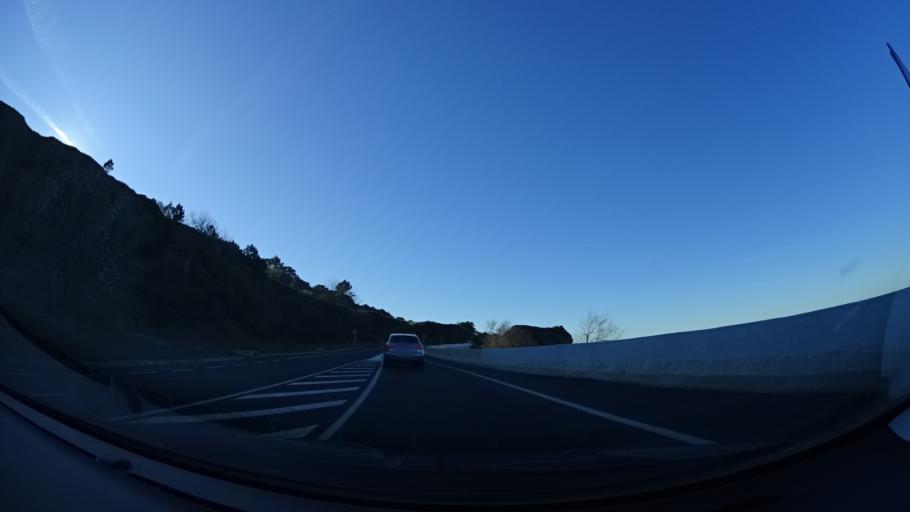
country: ES
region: Basque Country
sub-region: Provincia de Guipuzcoa
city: Getaria
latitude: 43.3099
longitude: -2.2236
